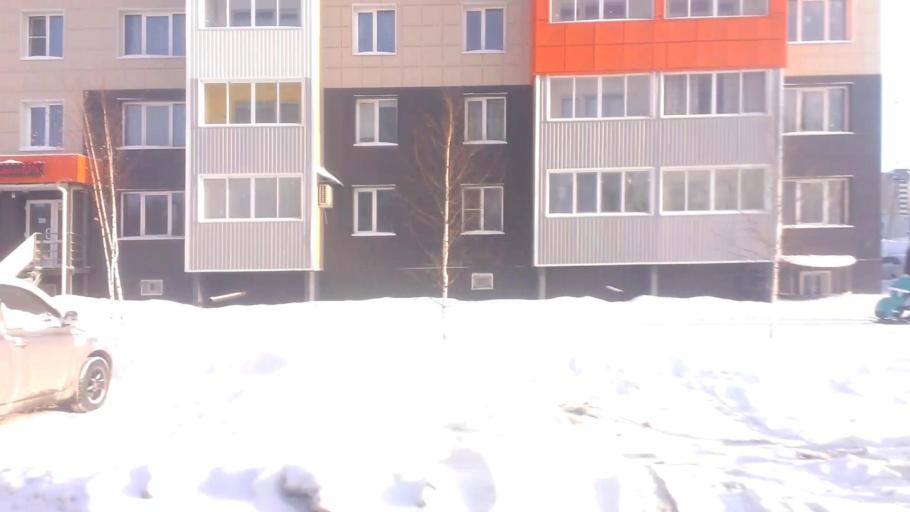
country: RU
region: Altai Krai
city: Novosilikatnyy
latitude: 53.3396
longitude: 83.6543
